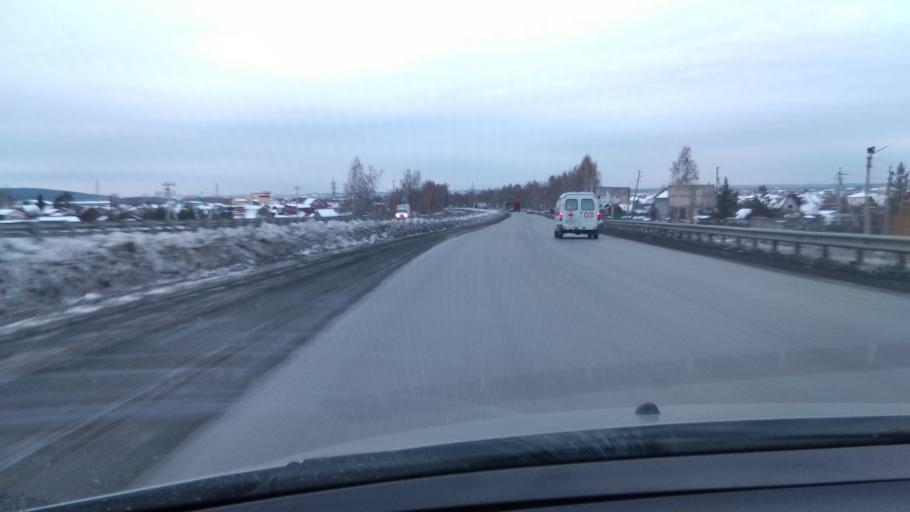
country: RU
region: Sverdlovsk
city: Aramil
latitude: 56.6978
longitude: 60.7502
